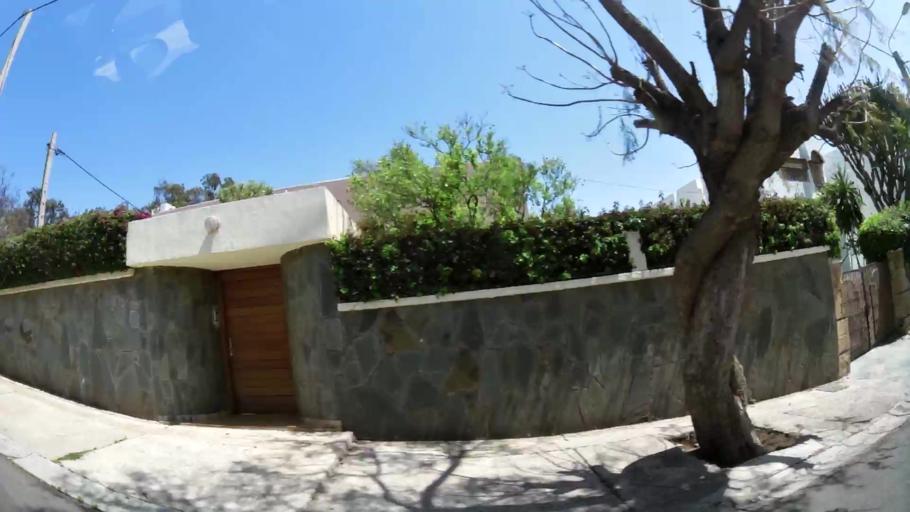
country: MA
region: Souss-Massa-Draa
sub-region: Agadir-Ida-ou-Tnan
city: Agadir
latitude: 30.4274
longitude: -9.5997
